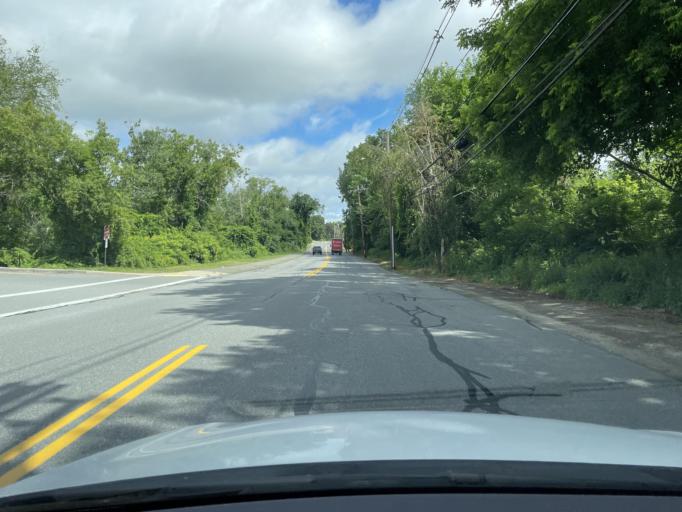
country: US
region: Massachusetts
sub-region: Middlesex County
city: Woburn
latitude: 42.4776
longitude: -71.1732
